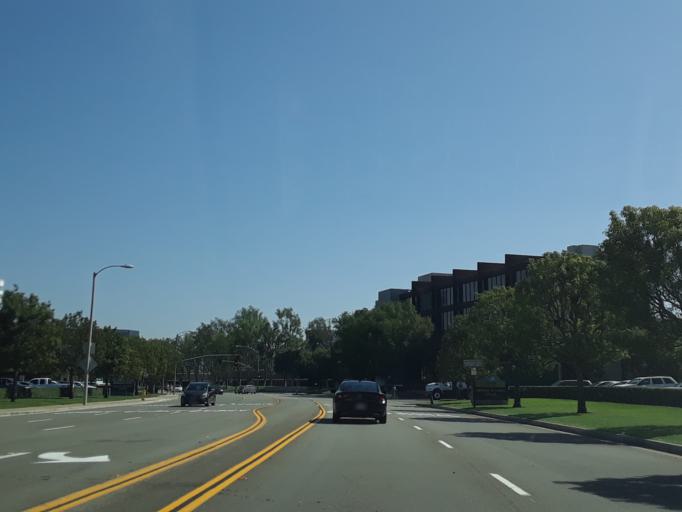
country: US
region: California
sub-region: Orange County
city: Irvine
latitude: 33.6773
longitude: -117.8599
